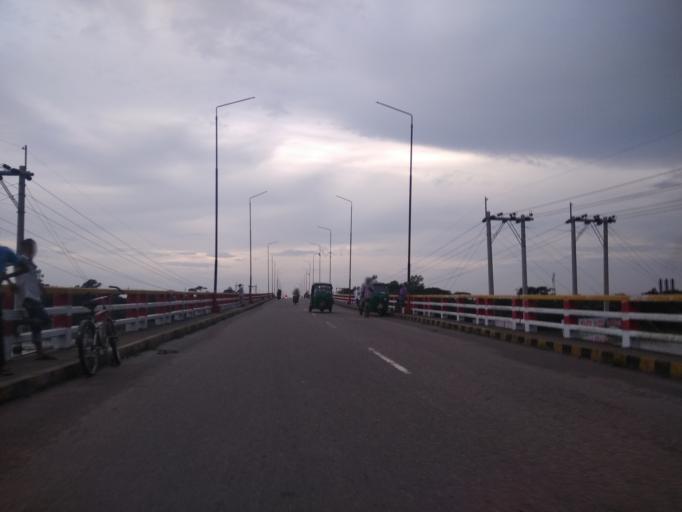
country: BD
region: Dhaka
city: Azimpur
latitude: 23.6697
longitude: 90.2899
